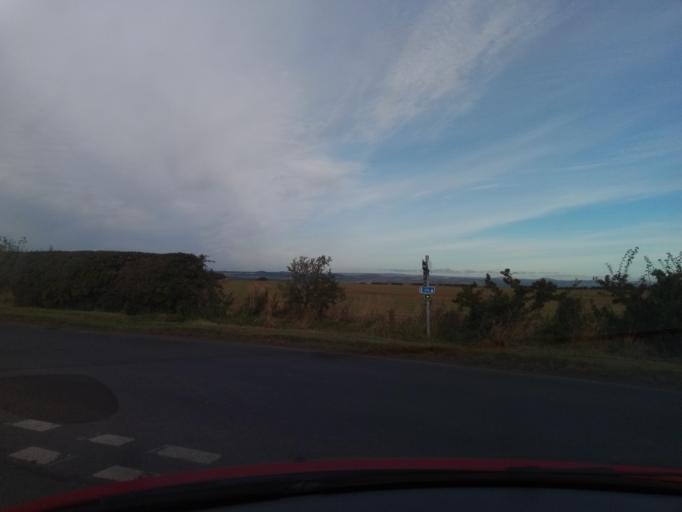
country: GB
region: Scotland
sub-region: The Scottish Borders
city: Kelso
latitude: 55.5870
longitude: -2.3755
